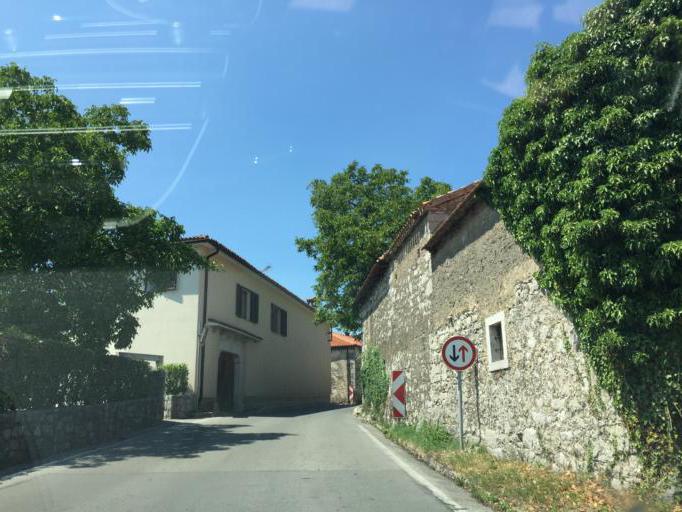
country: SI
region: Sezana
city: Sezana
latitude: 45.7541
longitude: 13.8561
